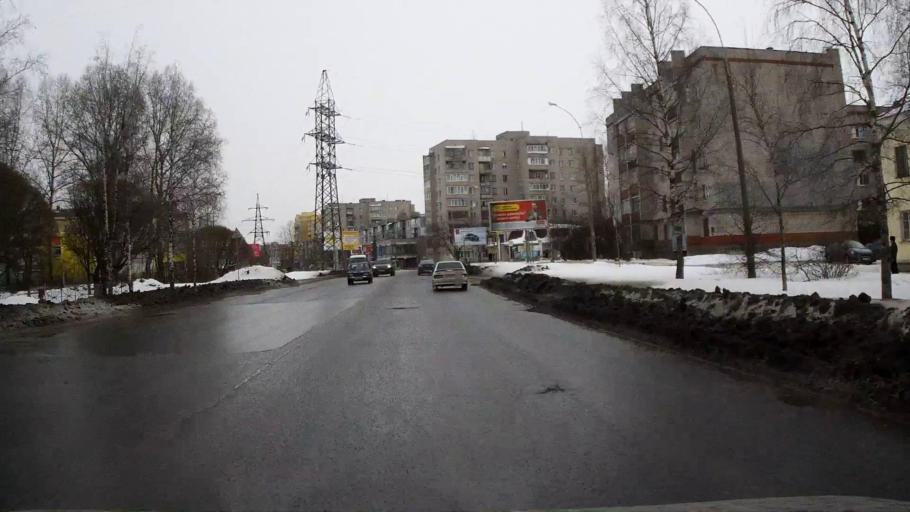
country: RU
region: Vologda
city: Vologda
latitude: 59.2165
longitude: 39.9193
